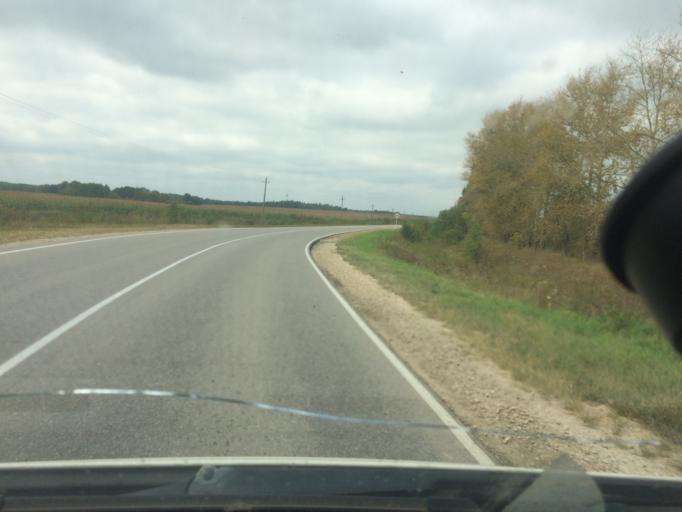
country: RU
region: Tula
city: Odoyev
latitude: 53.9914
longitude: 36.6951
